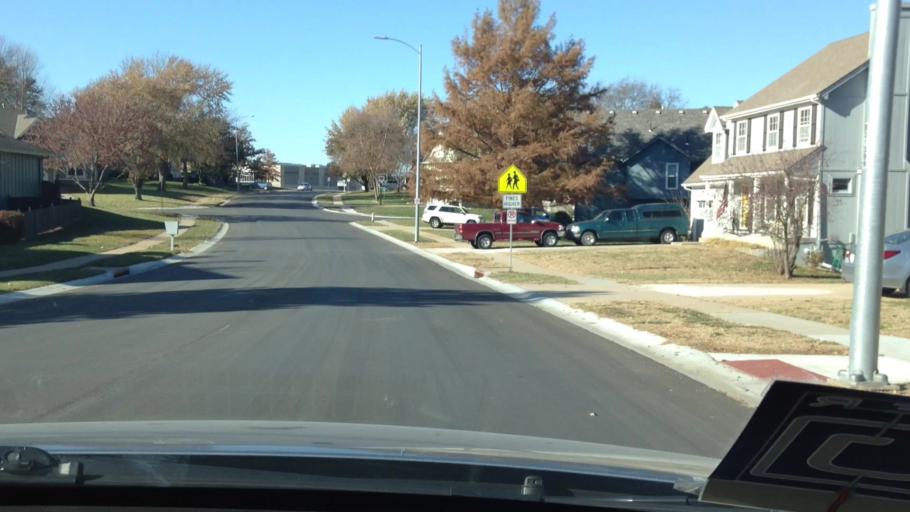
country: US
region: Kansas
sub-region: Johnson County
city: Olathe
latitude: 38.8936
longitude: -94.8649
